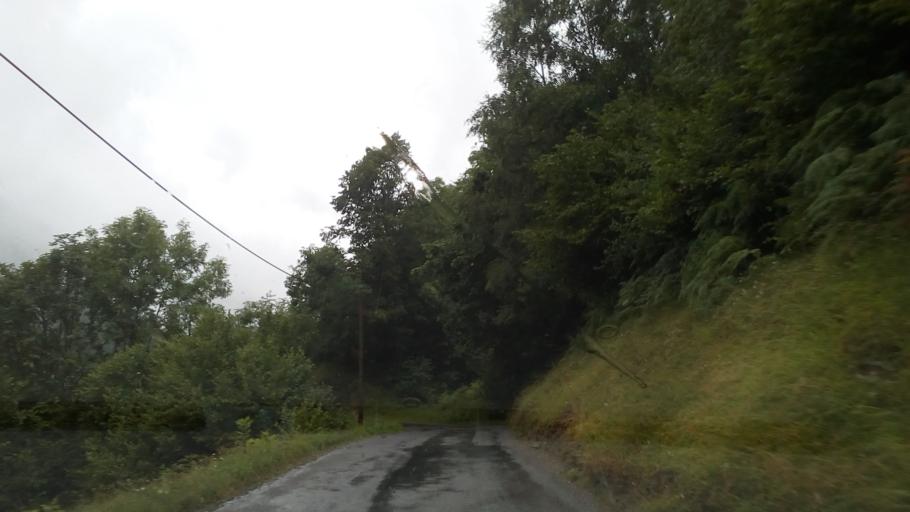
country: FR
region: Midi-Pyrenees
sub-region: Departement des Hautes-Pyrenees
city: Cauterets
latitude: 42.9449
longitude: -0.2275
